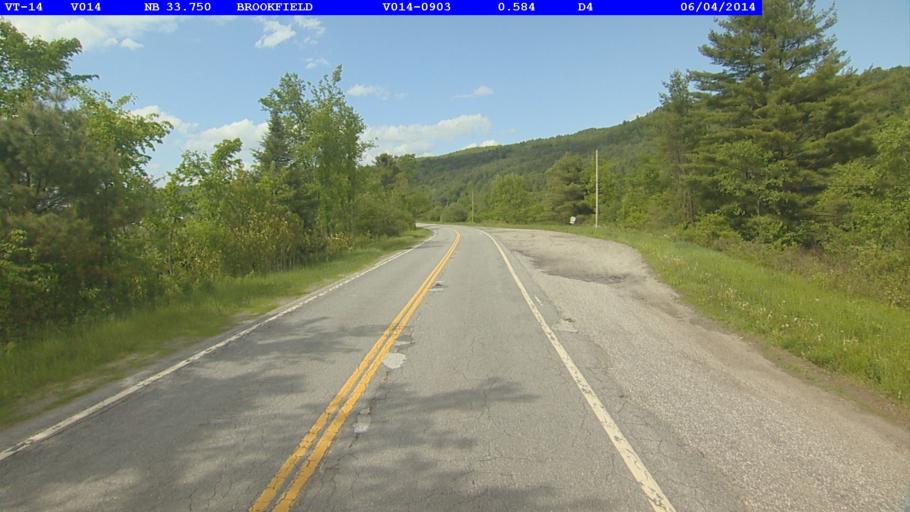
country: US
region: Vermont
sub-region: Orange County
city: Chelsea
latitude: 43.9874
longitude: -72.5567
